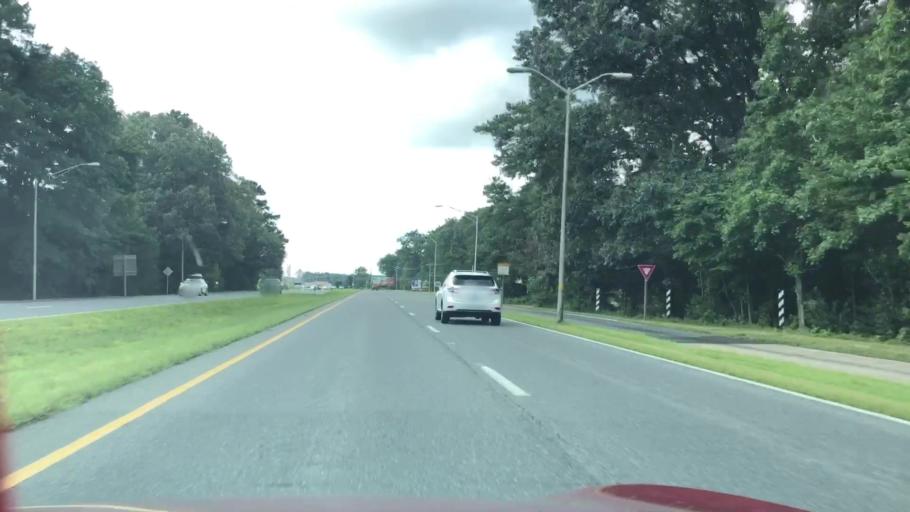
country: US
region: Virginia
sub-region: Accomack County
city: Wattsville
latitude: 37.9754
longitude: -75.5314
